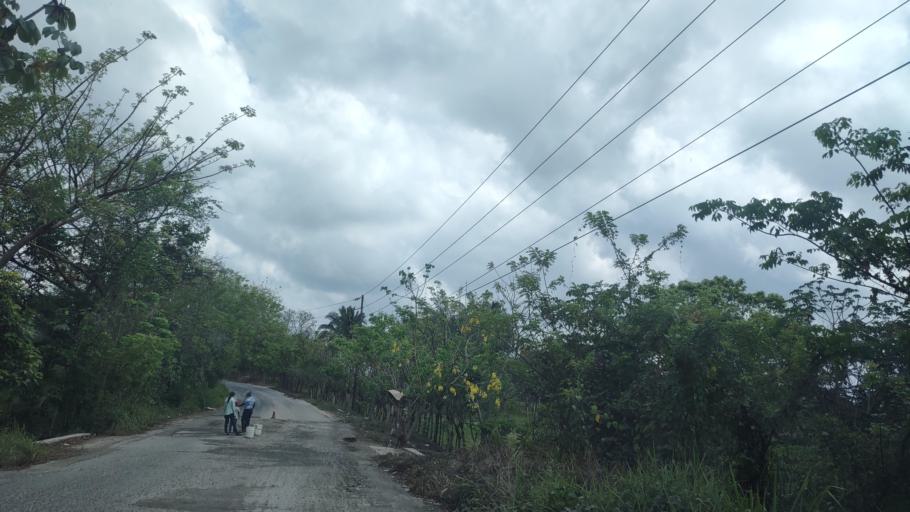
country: MX
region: Veracruz
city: Las Choapas
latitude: 17.9538
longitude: -94.1099
